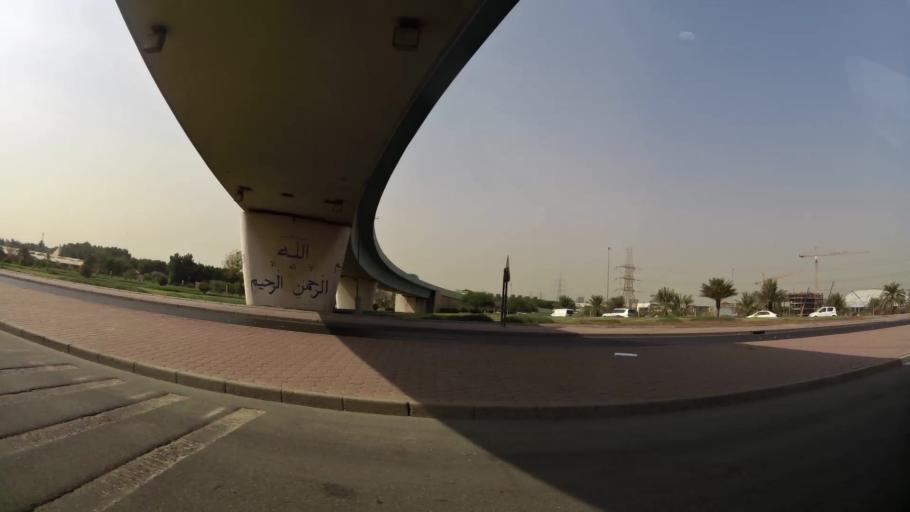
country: KW
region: Al Asimah
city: Ar Rabiyah
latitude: 29.3000
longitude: 47.9457
